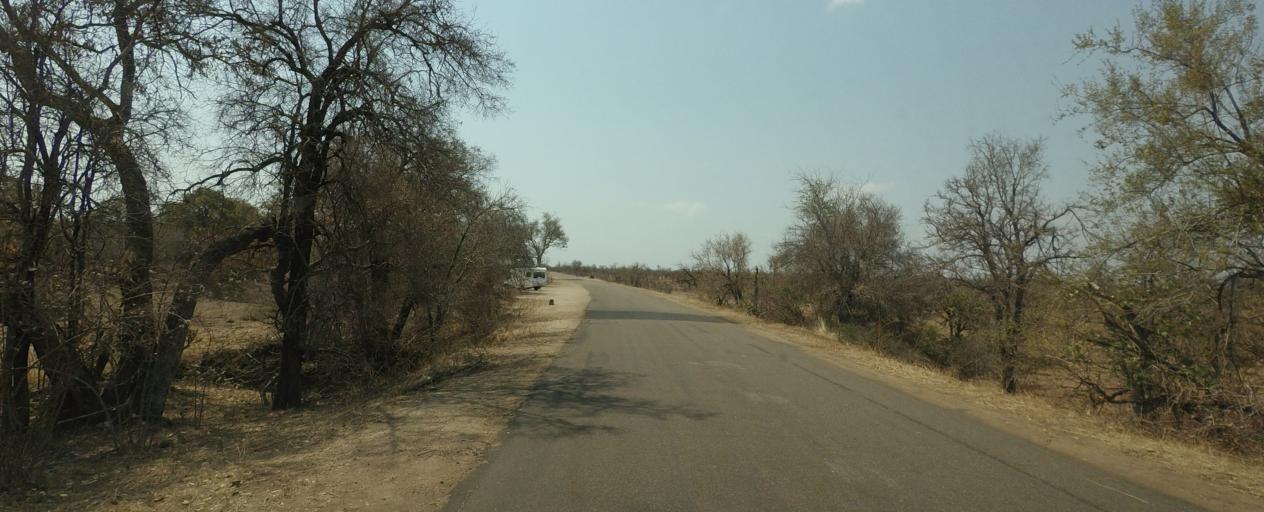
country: ZA
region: Limpopo
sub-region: Mopani District Municipality
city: Phalaborwa
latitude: -23.4159
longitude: 31.3396
